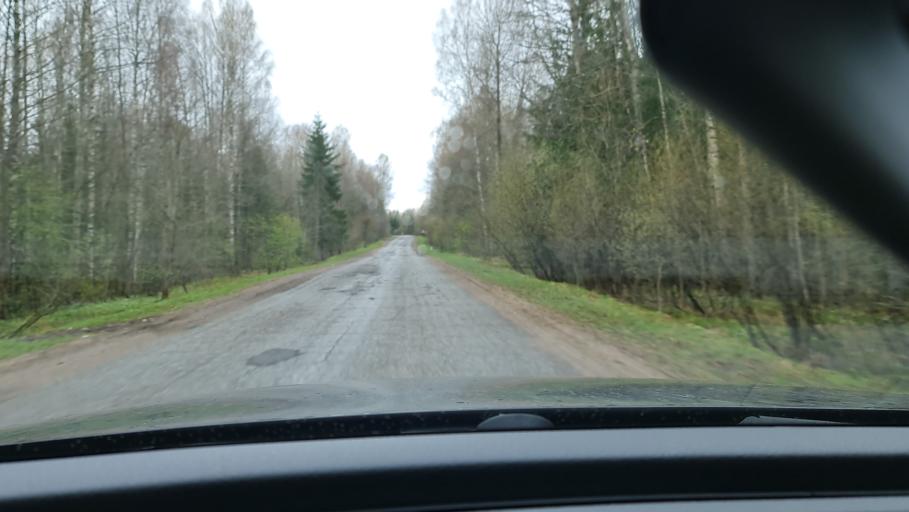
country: RU
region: Novgorod
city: Marevo
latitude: 57.2639
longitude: 32.0739
